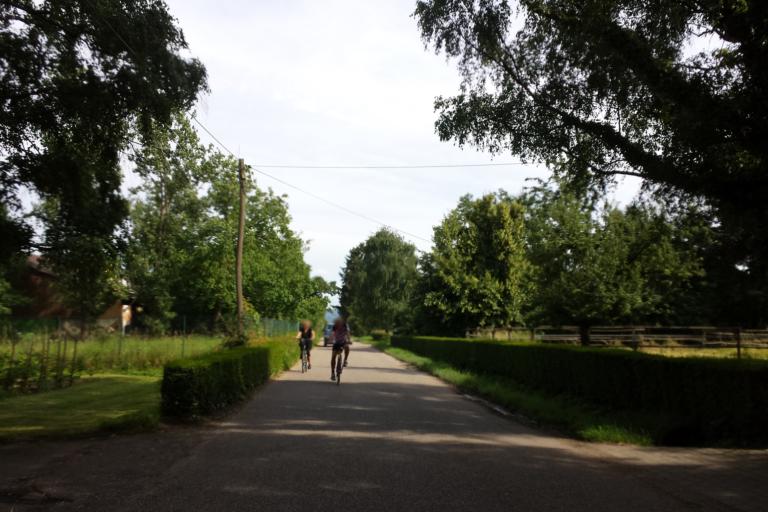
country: DE
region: Baden-Wuerttemberg
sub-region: Karlsruhe Region
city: Edingen-Neckarhausen
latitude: 49.4563
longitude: 8.6271
